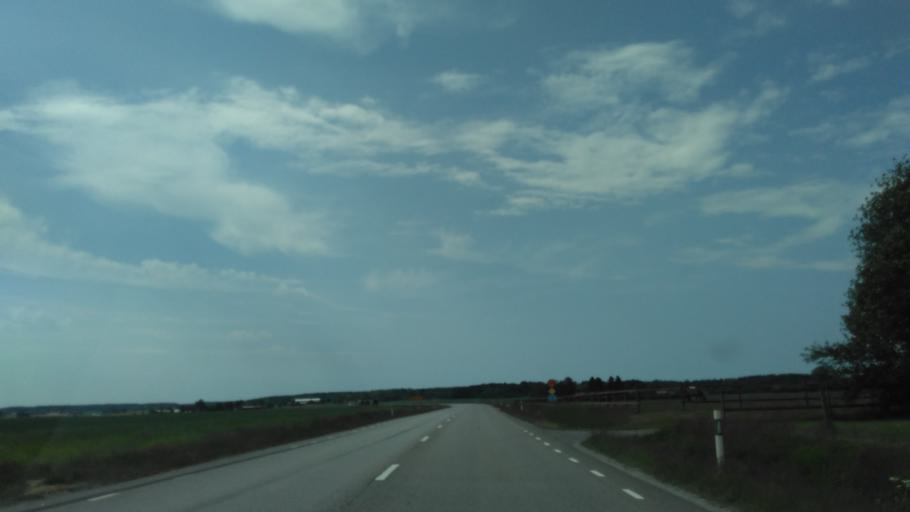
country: SE
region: Vaestra Goetaland
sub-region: Lidkopings Kommun
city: Lidkoping
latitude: 58.4800
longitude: 13.0899
